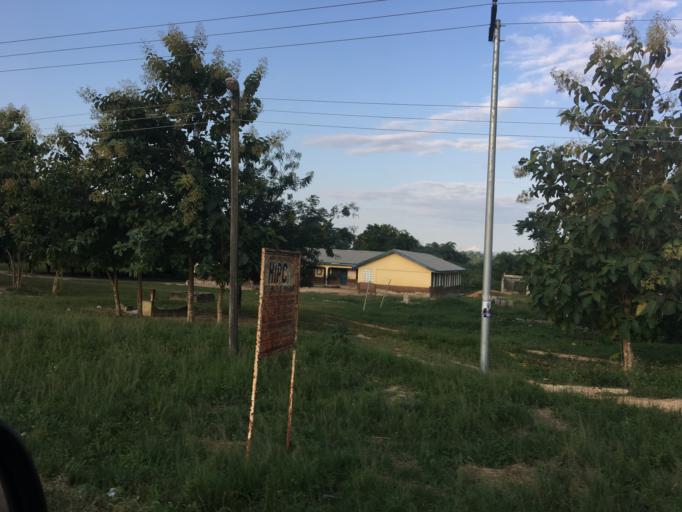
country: GH
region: Western
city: Bibiani
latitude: 6.6145
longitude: -2.4083
